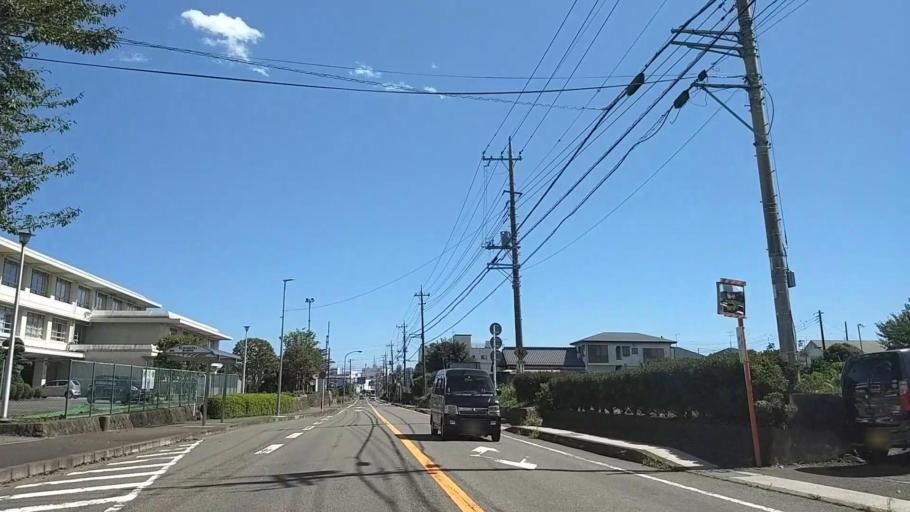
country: JP
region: Kanagawa
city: Zama
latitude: 35.5318
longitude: 139.3164
